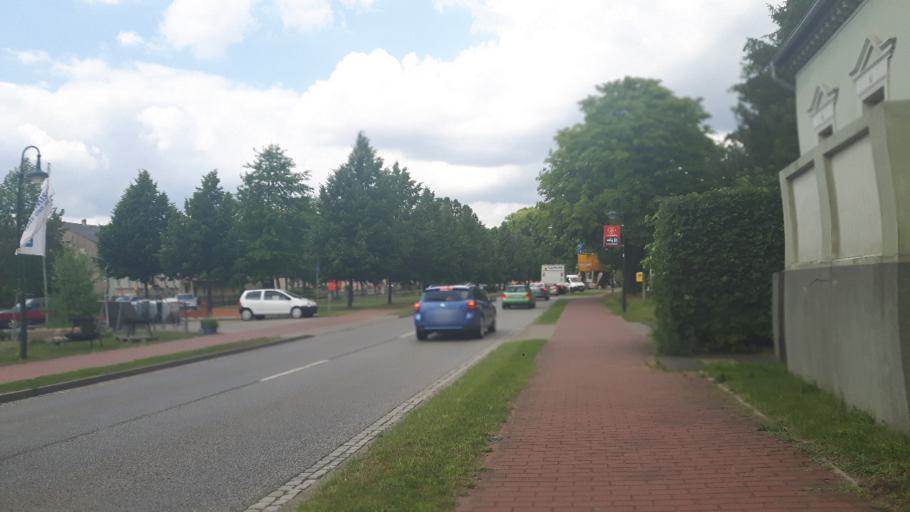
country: DE
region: Berlin
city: Buch
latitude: 52.6227
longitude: 13.5433
